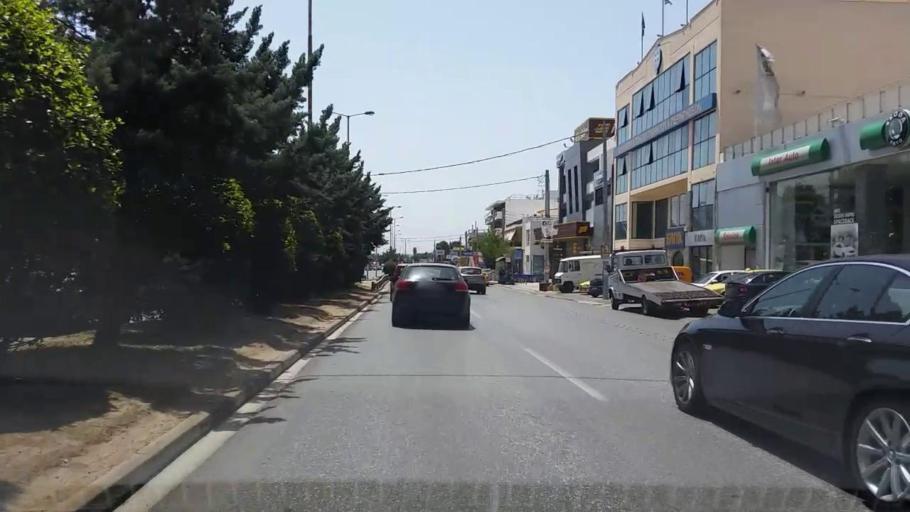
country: GR
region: Attica
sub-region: Nomarchia Athinas
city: Khalandrion
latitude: 38.0121
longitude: 23.8145
